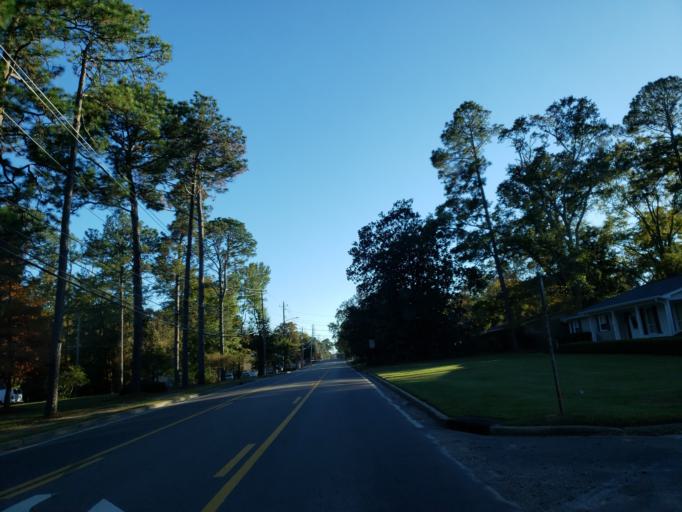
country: US
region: Mississippi
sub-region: Forrest County
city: Hattiesburg
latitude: 31.3152
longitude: -89.3313
